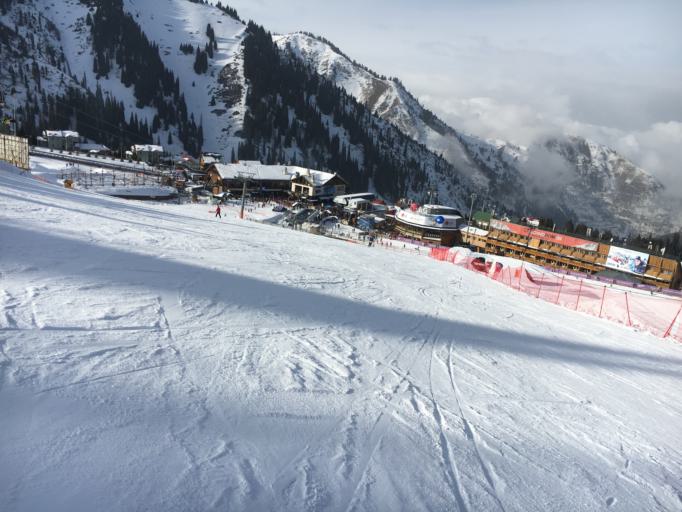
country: KZ
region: Almaty Qalasy
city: Almaty
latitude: 43.1269
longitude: 77.0841
